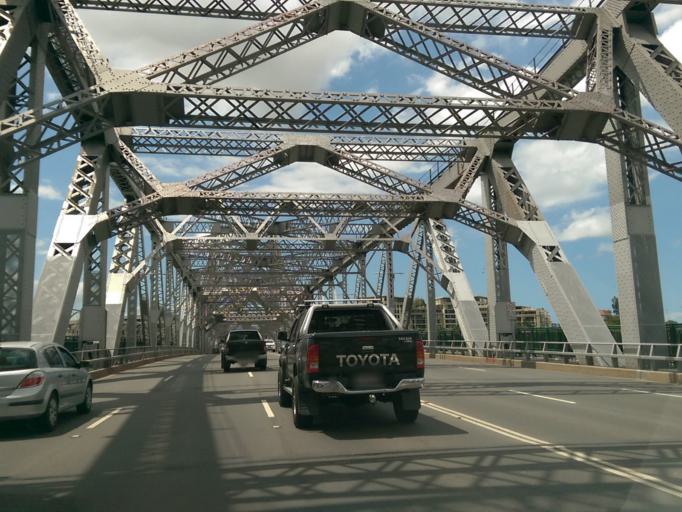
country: AU
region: Queensland
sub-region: Brisbane
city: Fortitude Valley
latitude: -27.4645
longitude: 153.0358
